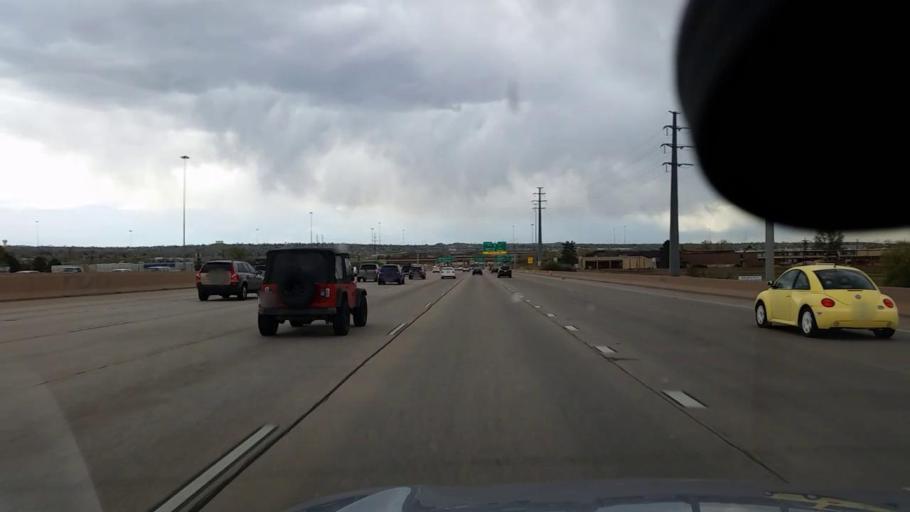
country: US
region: Colorado
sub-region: Adams County
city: Twin Lakes
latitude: 39.8100
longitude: -104.9827
